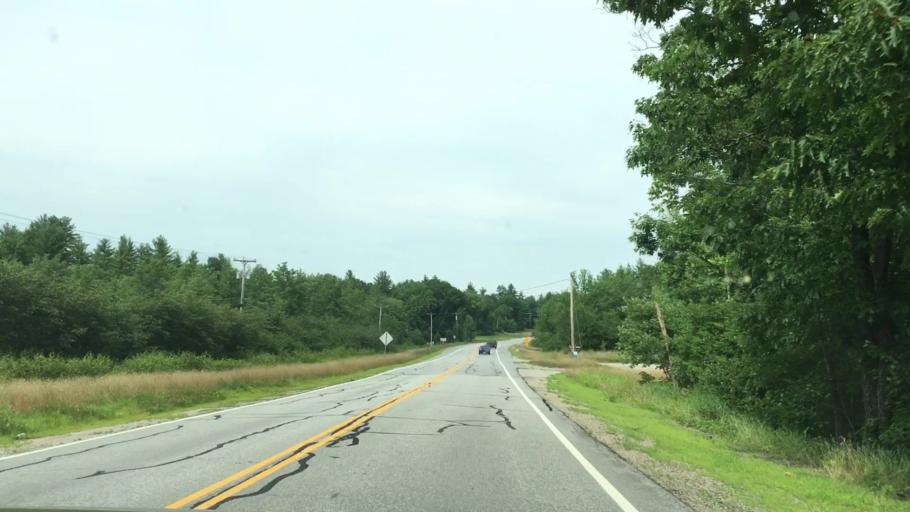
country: US
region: New Hampshire
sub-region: Hillsborough County
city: Antrim
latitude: 43.0427
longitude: -71.9339
